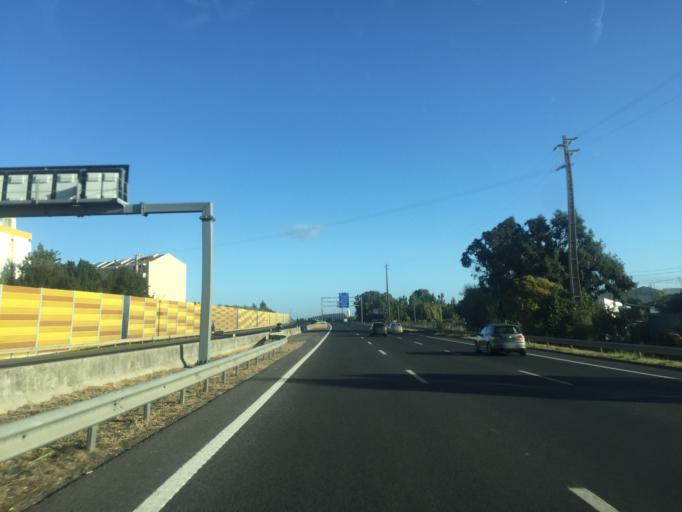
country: PT
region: Lisbon
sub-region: Vila Franca de Xira
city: Castanheira do Ribatejo
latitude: 38.9880
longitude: -8.9706
